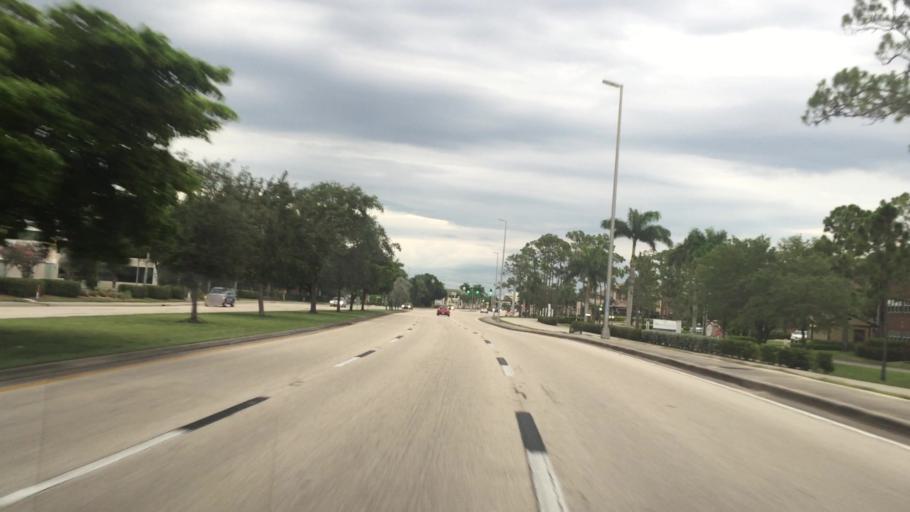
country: US
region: Florida
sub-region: Lee County
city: Whiskey Creek
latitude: 26.5566
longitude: -81.8958
